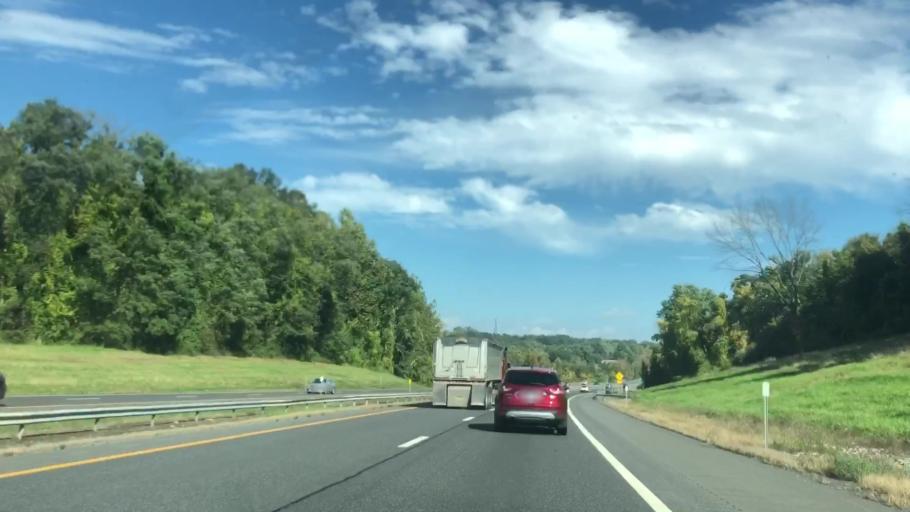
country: US
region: New York
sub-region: Ulster County
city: Rosendale Village
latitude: 41.8485
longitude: -74.0597
